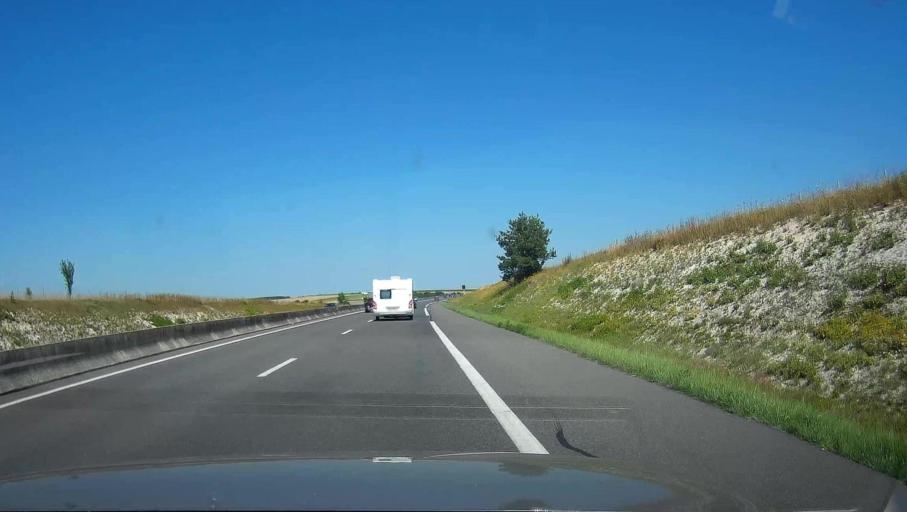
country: FR
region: Champagne-Ardenne
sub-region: Departement de l'Aube
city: Mailly-le-Camp
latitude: 48.6666
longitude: 4.1703
